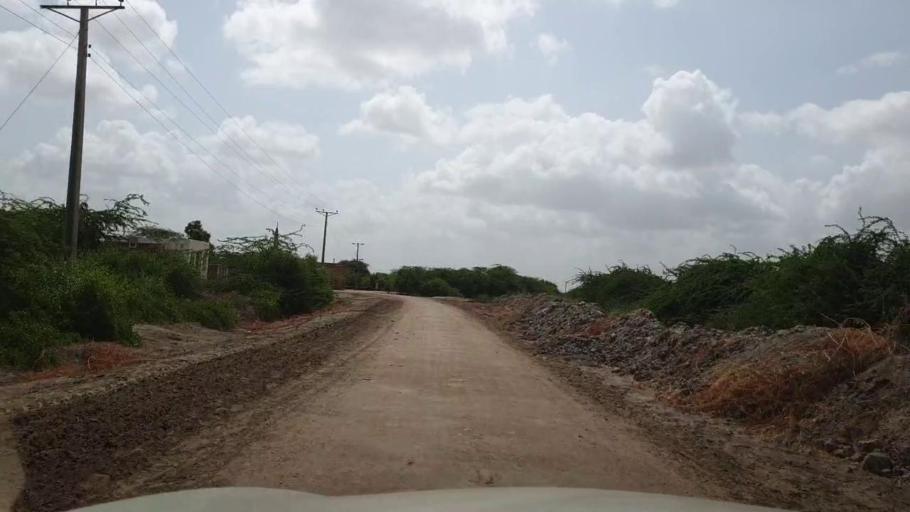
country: PK
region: Sindh
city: Kadhan
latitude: 24.3886
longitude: 68.7934
